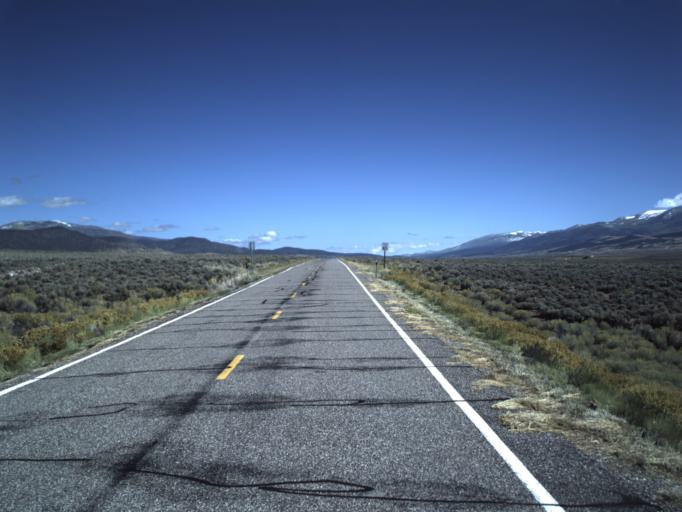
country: US
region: Utah
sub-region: Wayne County
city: Loa
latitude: 38.3721
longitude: -111.9386
